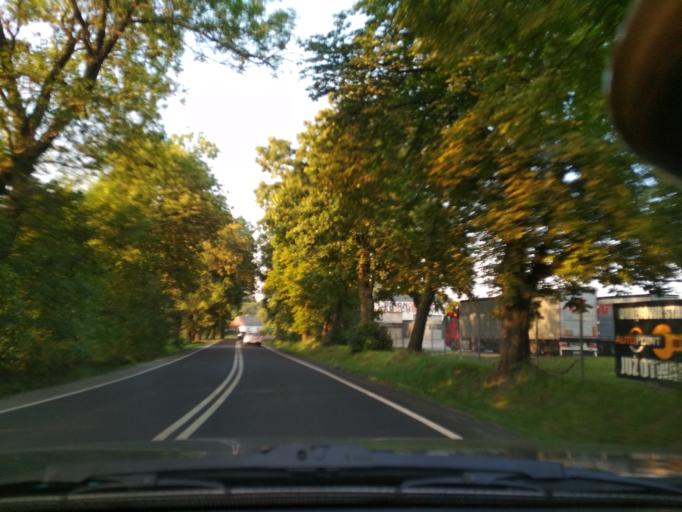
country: PL
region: Silesian Voivodeship
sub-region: Powiat zawiercianski
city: Pilica
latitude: 50.4700
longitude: 19.6293
